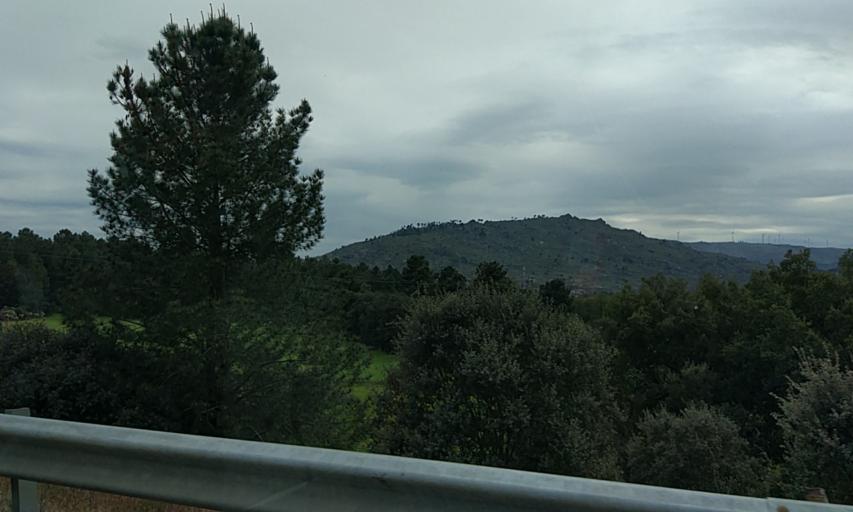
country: PT
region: Guarda
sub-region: Celorico da Beira
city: Celorico da Beira
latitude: 40.6359
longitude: -7.3204
